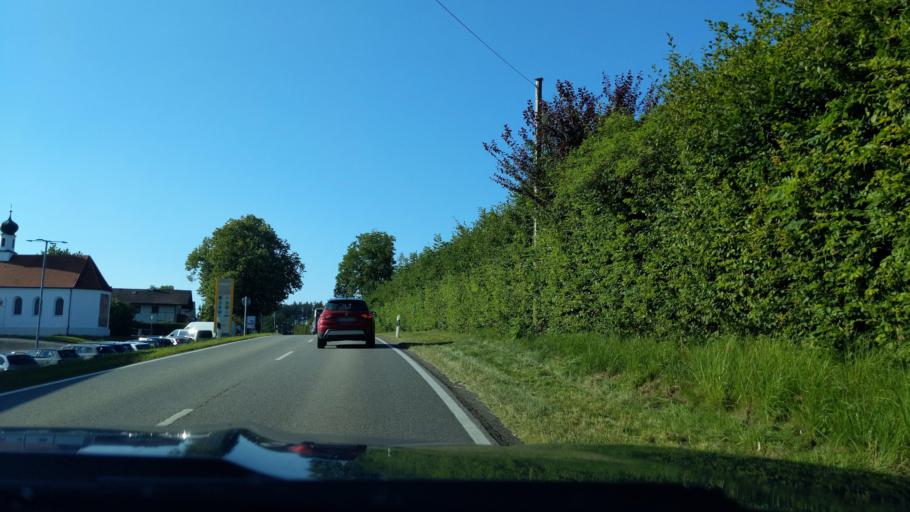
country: DE
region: Bavaria
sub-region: Upper Bavaria
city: Tuntenhausen
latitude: 47.9382
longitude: 11.9810
